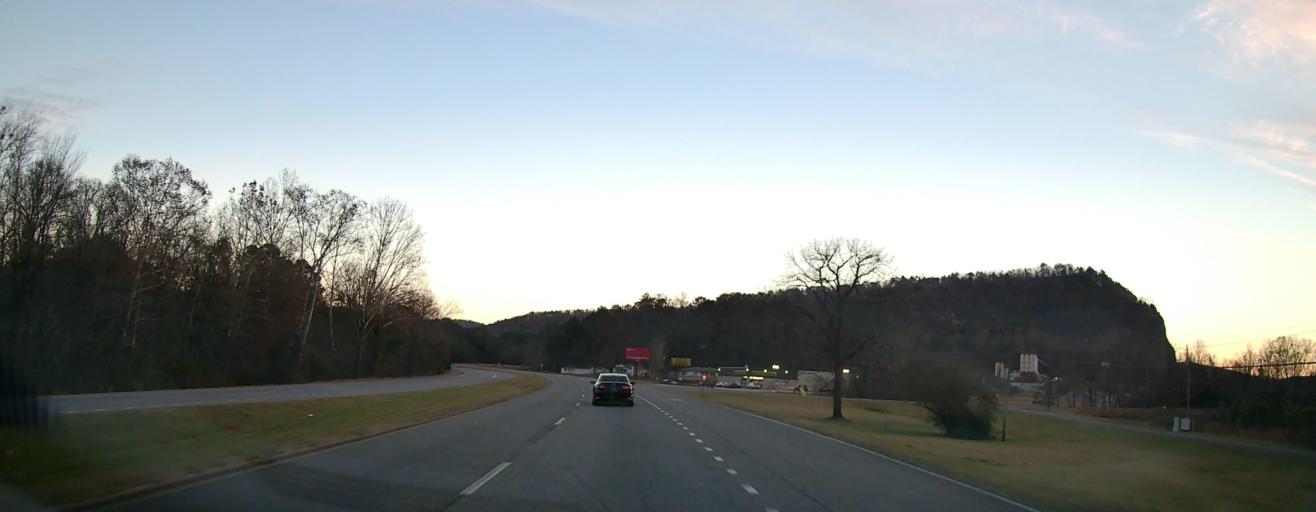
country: US
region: Alabama
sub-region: Etowah County
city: Glencoe
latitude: 33.9486
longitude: -85.9281
